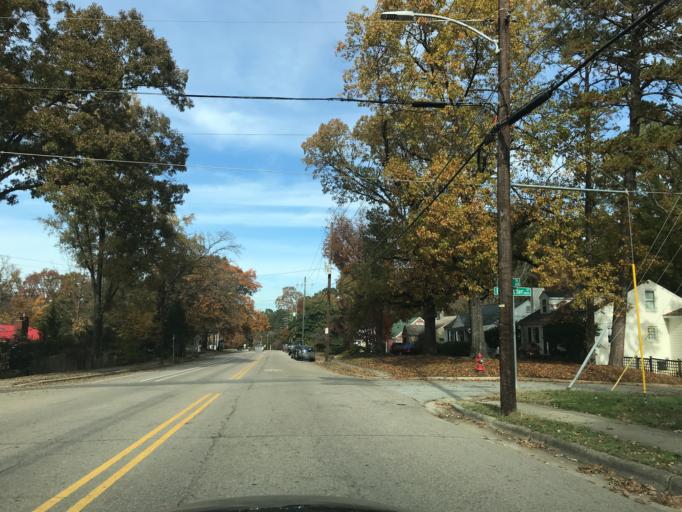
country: US
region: North Carolina
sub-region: Wake County
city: West Raleigh
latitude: 35.7984
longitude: -78.6766
